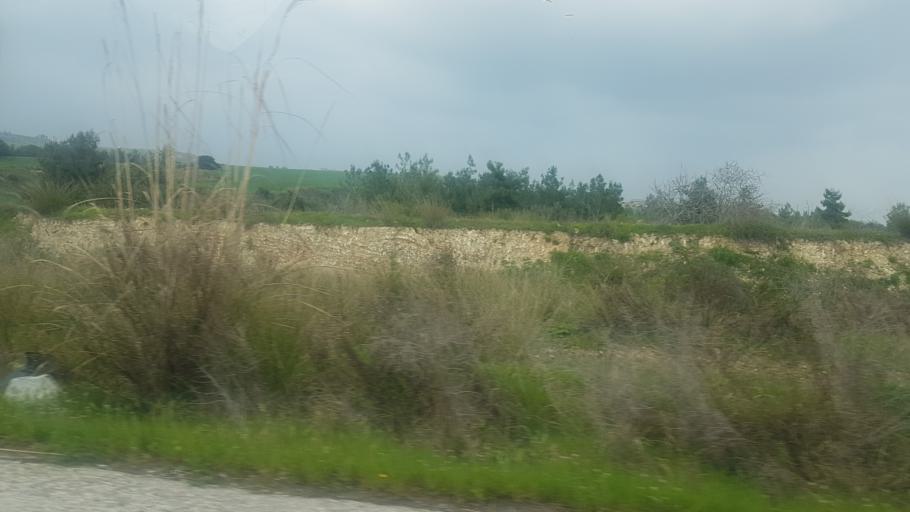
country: TR
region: Adana
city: Seyhan
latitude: 37.0439
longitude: 35.1831
